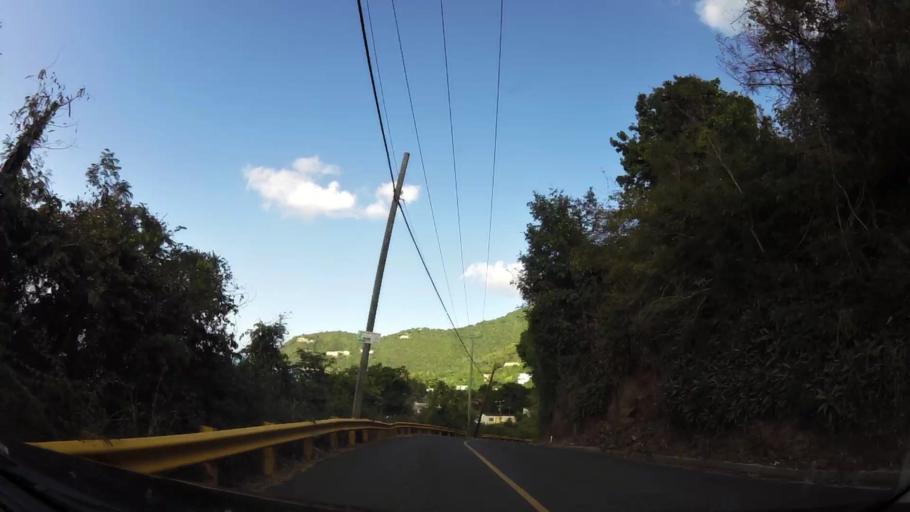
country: VG
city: Road Town
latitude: 18.4042
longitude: -64.6759
